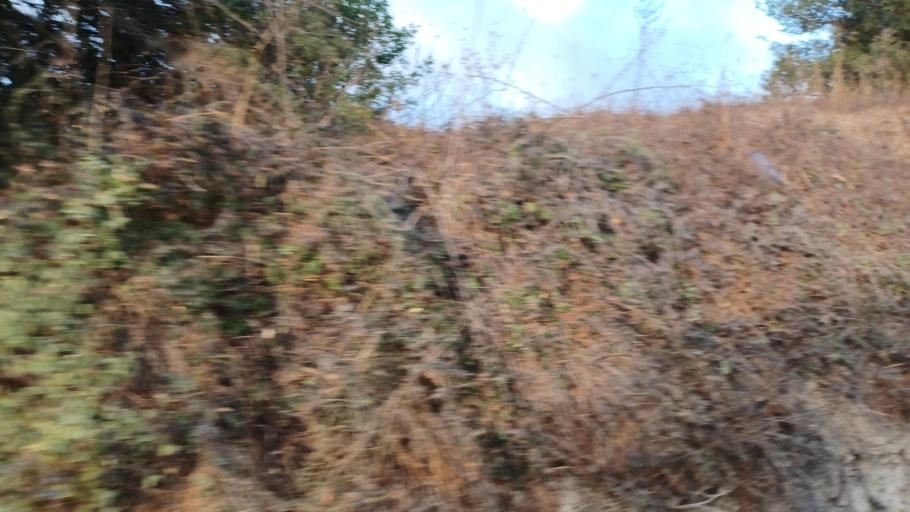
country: CY
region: Pafos
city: Mesogi
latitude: 34.8213
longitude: 32.5801
